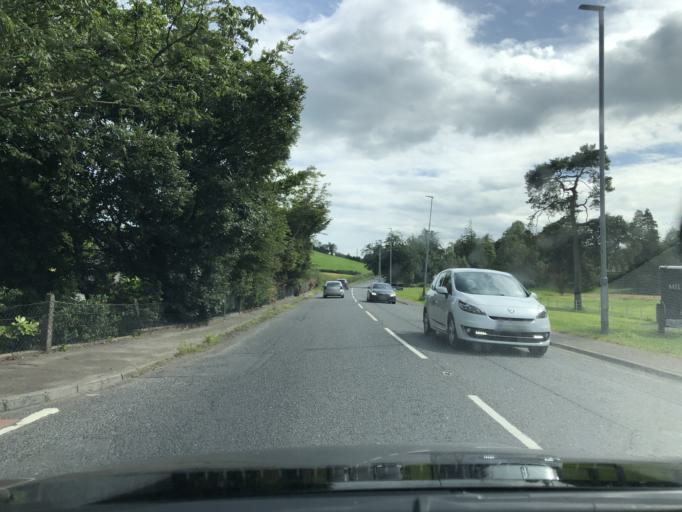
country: GB
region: Northern Ireland
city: Ballynahinch
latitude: 54.3934
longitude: -5.8844
